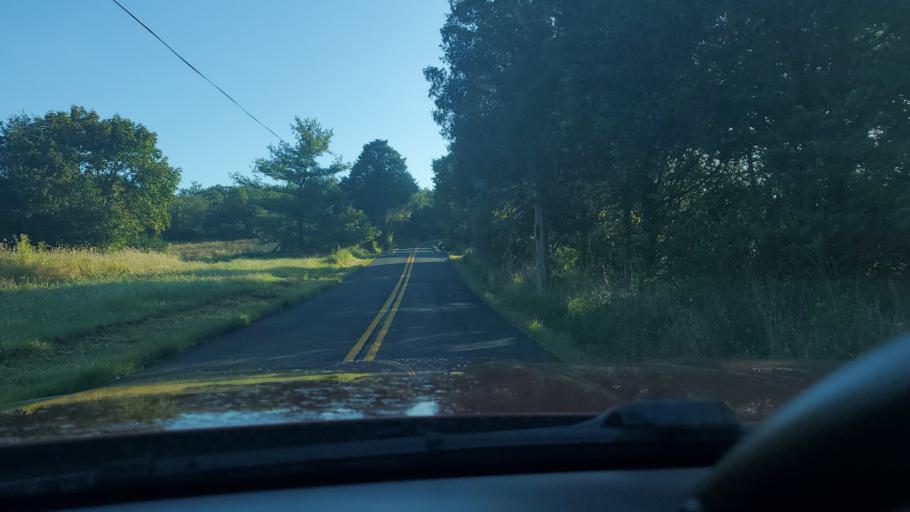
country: US
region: Pennsylvania
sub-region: Montgomery County
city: Woxall
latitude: 40.2934
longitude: -75.4431
